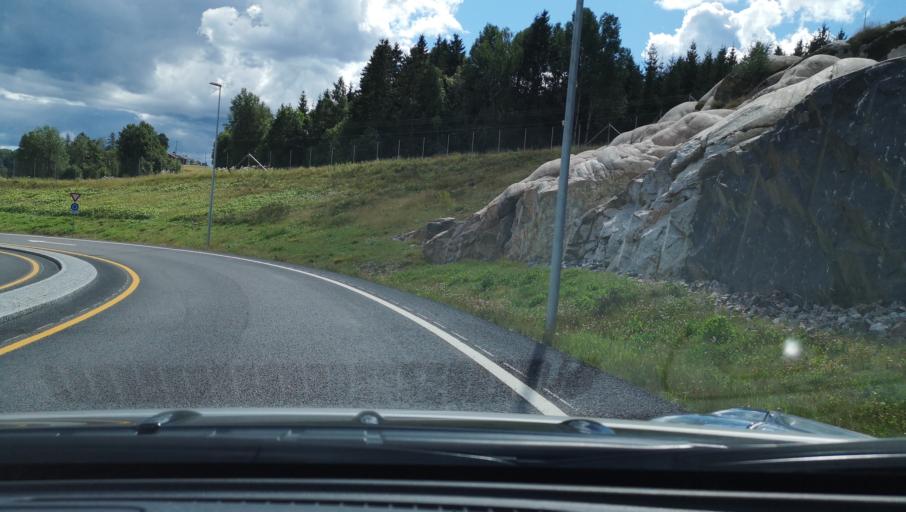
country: NO
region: Ostfold
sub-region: Hobol
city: Elvestad
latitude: 59.6284
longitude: 10.9519
